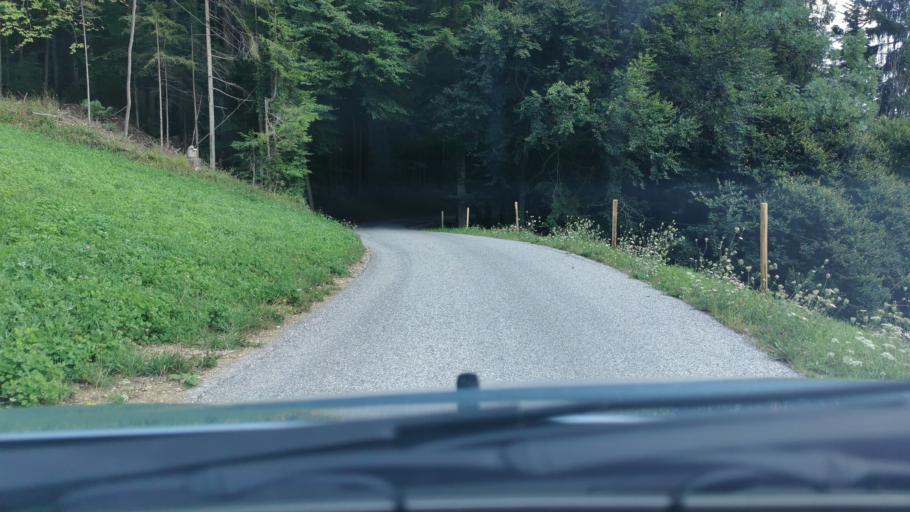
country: AT
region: Styria
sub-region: Politischer Bezirk Weiz
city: Koglhof
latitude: 47.3233
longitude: 15.6656
